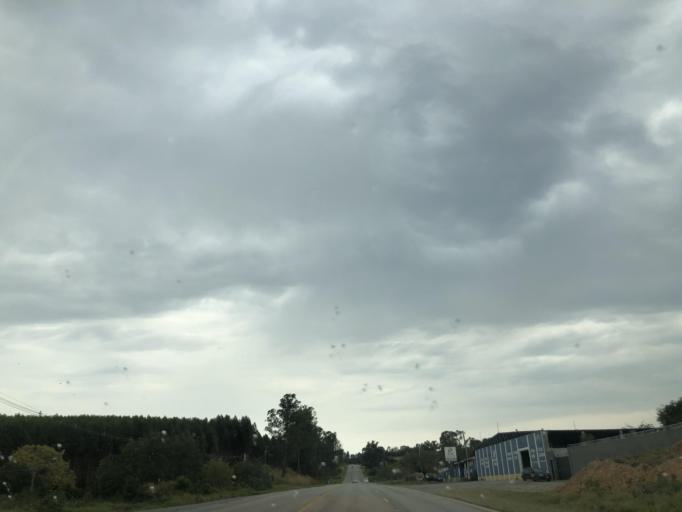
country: BR
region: Sao Paulo
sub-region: Salto De Pirapora
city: Salto de Pirapora
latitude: -23.6985
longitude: -47.6173
